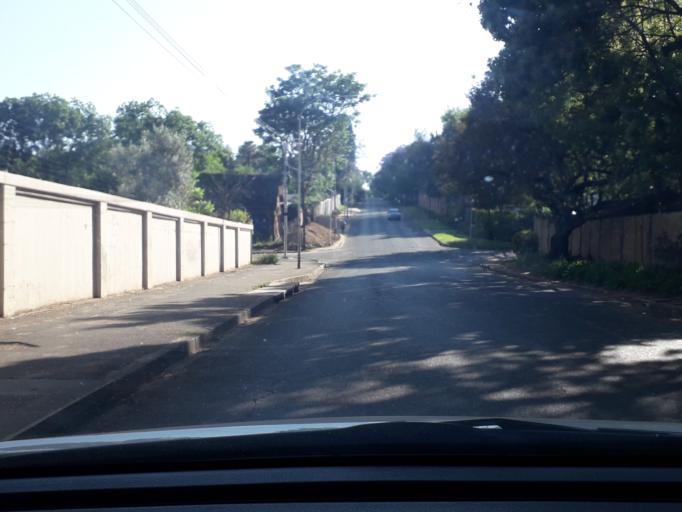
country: ZA
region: Gauteng
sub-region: City of Johannesburg Metropolitan Municipality
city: Johannesburg
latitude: -26.1154
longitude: 28.0247
